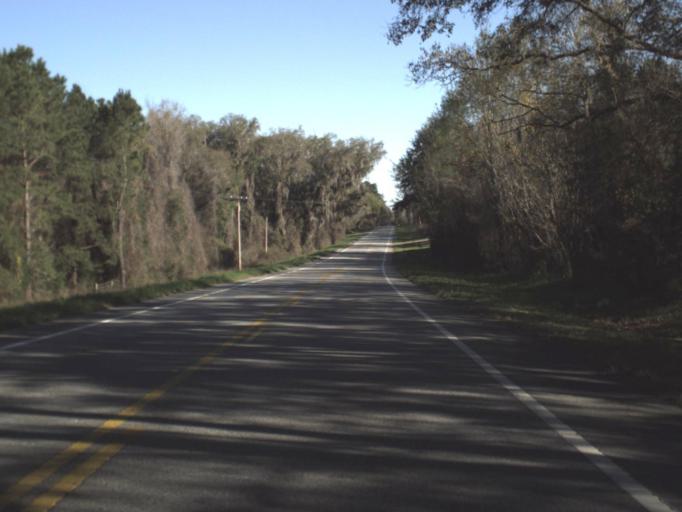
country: US
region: Georgia
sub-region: Brooks County
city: Quitman
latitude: 30.5707
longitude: -83.6373
